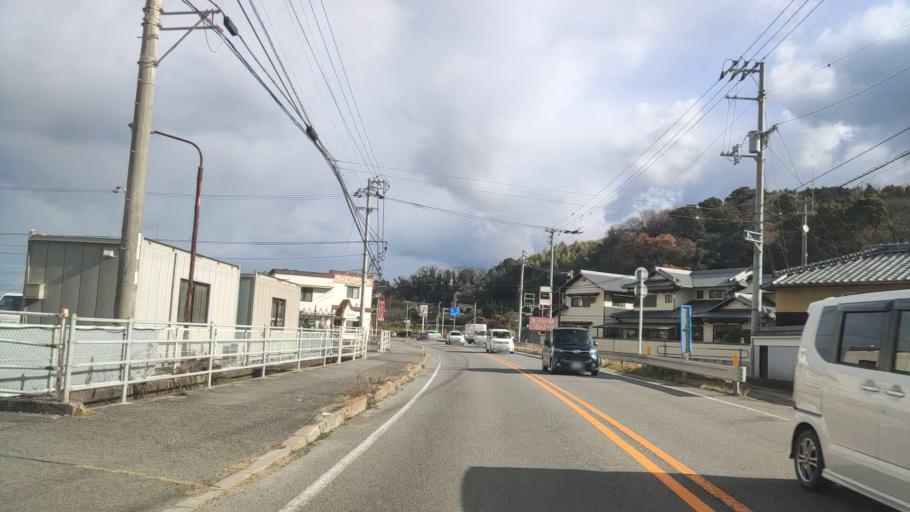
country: JP
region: Ehime
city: Hojo
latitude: 34.0389
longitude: 132.8459
